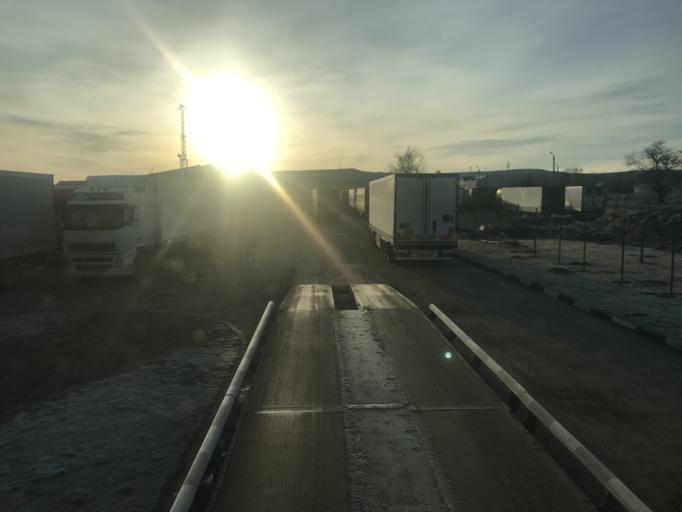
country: AZ
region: Qusar
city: Samur
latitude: 41.6410
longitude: 48.4057
